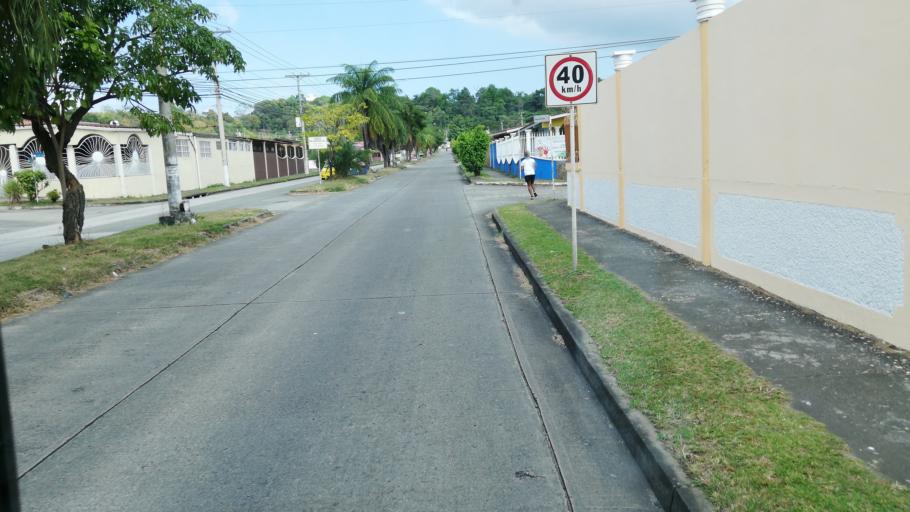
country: PA
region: Panama
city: San Miguelito
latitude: 9.0596
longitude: -79.4598
